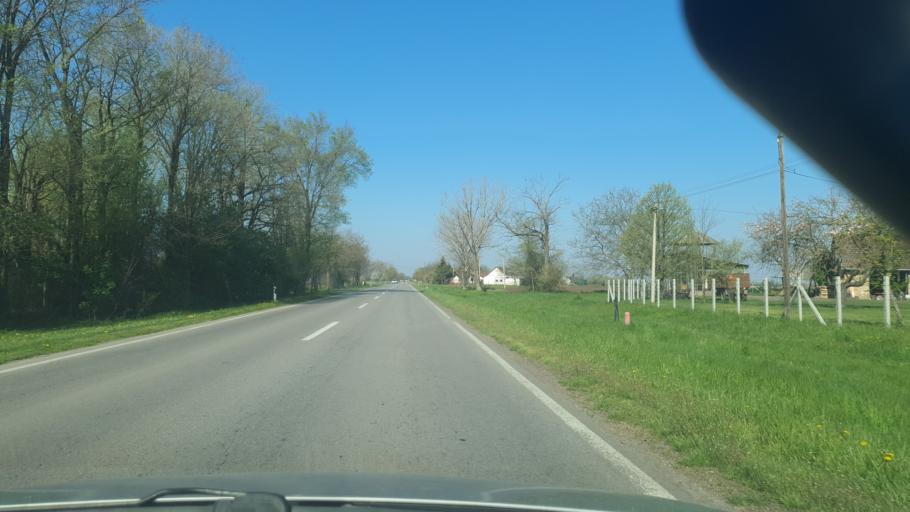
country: RS
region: Autonomna Pokrajina Vojvodina
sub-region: Zapadnobacki Okrug
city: Sombor
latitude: 45.7685
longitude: 19.1805
